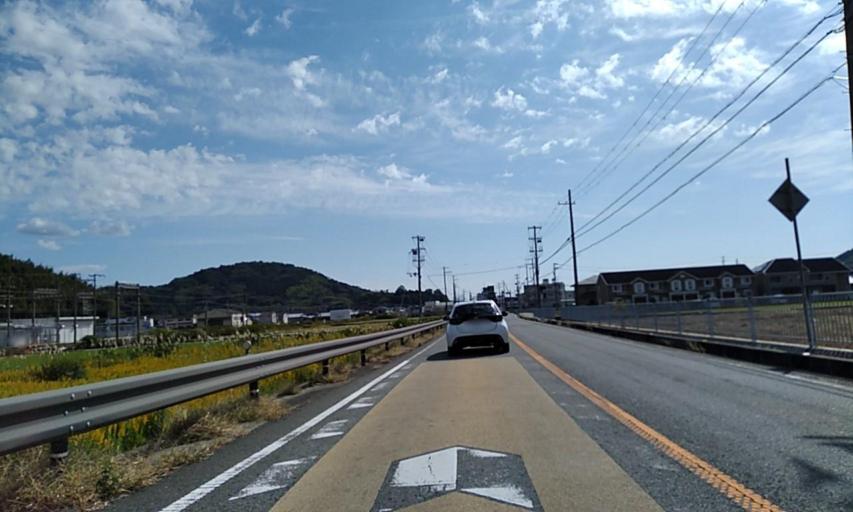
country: JP
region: Wakayama
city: Gobo
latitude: 33.9212
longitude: 135.1459
